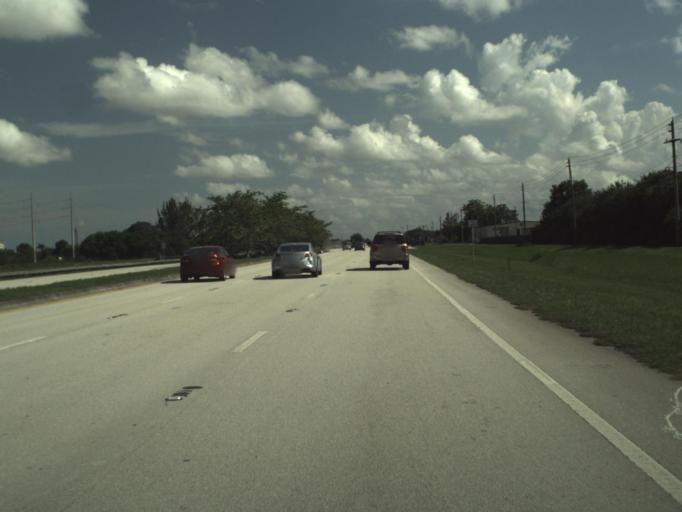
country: US
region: Florida
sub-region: Palm Beach County
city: Villages of Oriole
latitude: 26.5415
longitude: -80.2057
